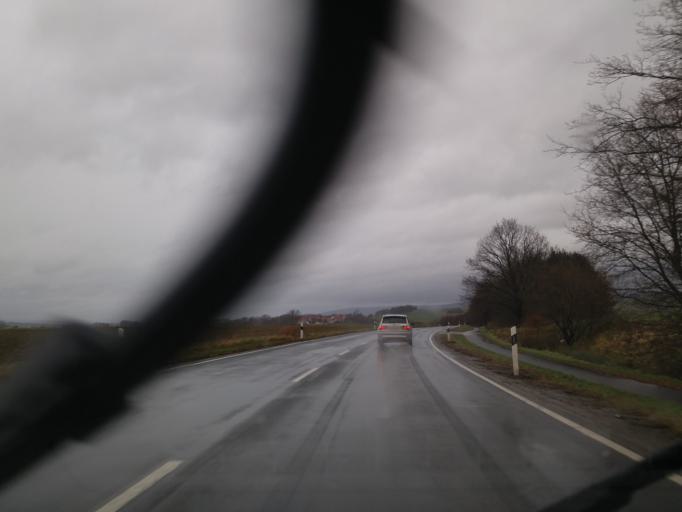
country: DE
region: Lower Saxony
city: Gemeinde Friedland
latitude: 51.4444
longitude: 9.9307
